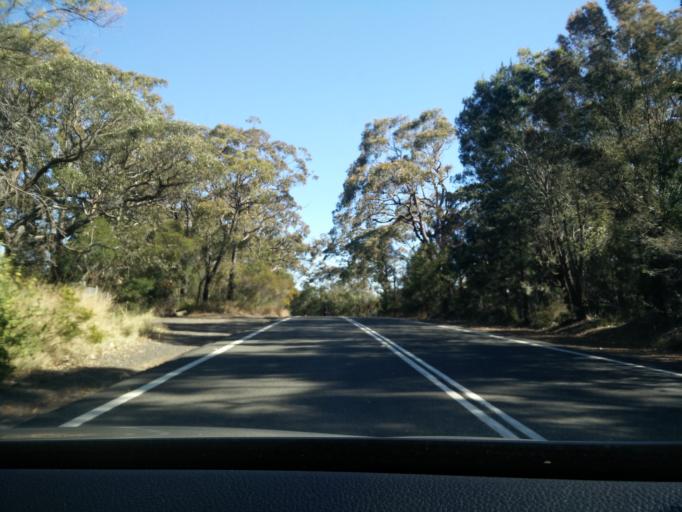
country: AU
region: New South Wales
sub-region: Hornsby Shire
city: Berowra
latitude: -33.5985
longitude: 151.1653
